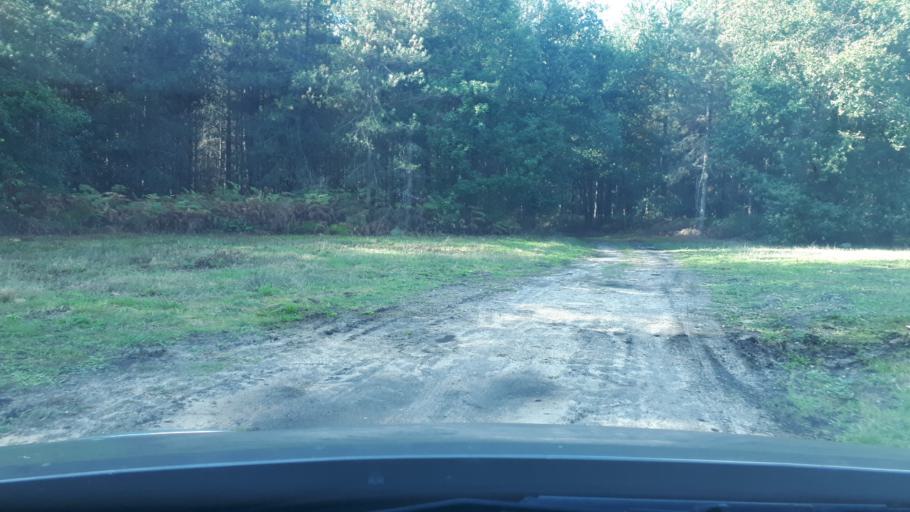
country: FR
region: Centre
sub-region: Departement du Loir-et-Cher
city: Saint-Romain-sur-Cher
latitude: 47.3477
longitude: 1.3641
